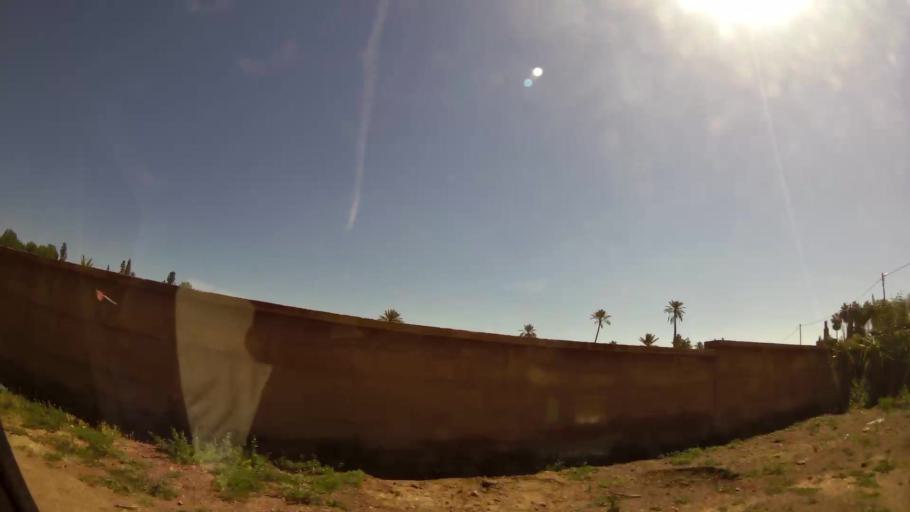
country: MA
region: Marrakech-Tensift-Al Haouz
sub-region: Marrakech
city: Marrakesh
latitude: 31.6657
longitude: -7.9599
